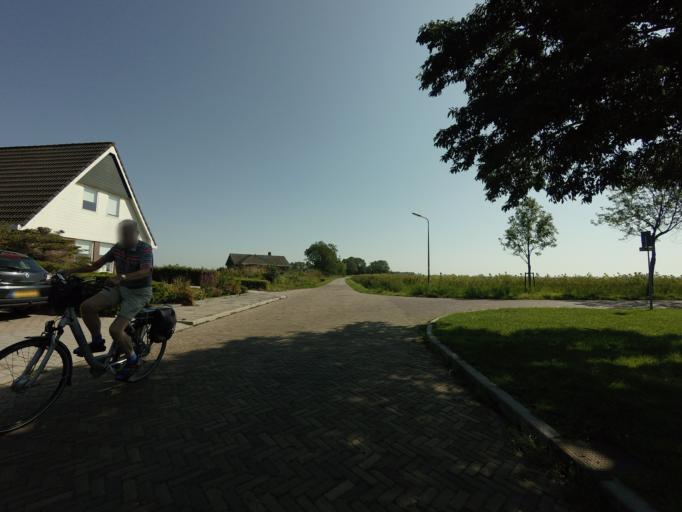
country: NL
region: Friesland
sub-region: Gemeente Dongeradeel
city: Holwerd
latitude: 53.3673
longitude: 5.9085
